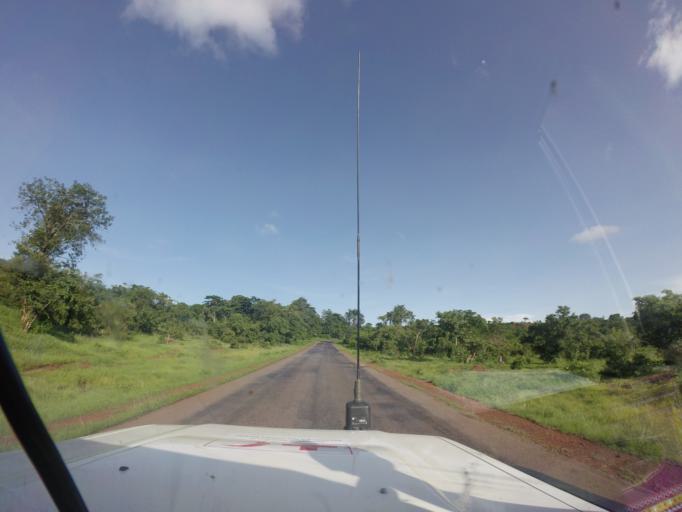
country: GN
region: Kindia
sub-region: Kindia
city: Kindia
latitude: 10.0604
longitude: -12.6548
